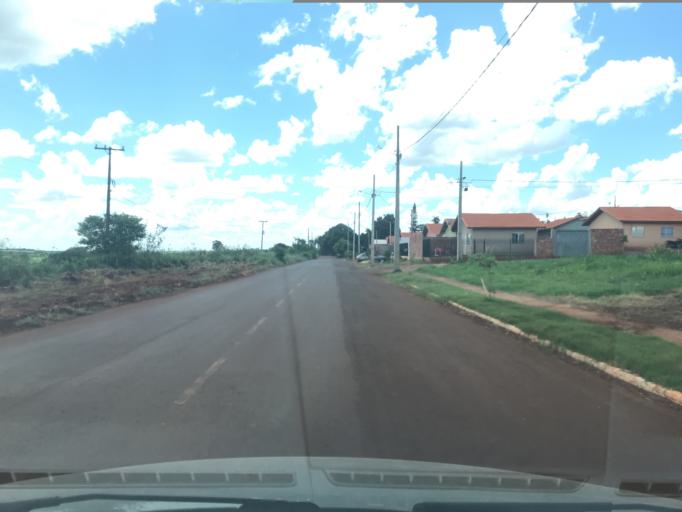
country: BR
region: Parana
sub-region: Palotina
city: Palotina
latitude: -24.2662
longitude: -53.8485
